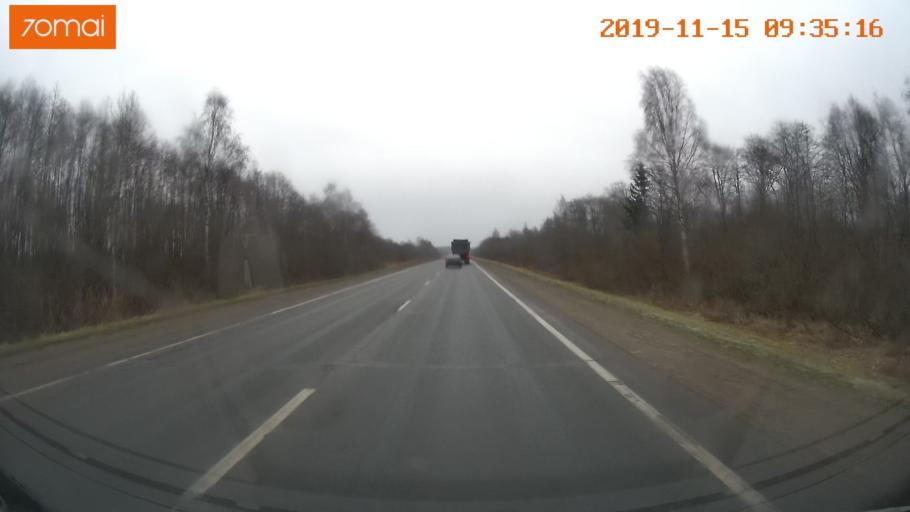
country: RU
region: Vologda
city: Sheksna
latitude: 59.2554
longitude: 38.3955
